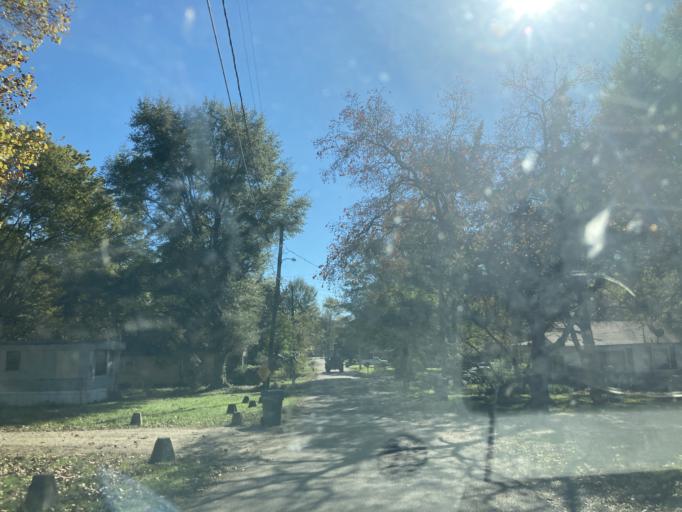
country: US
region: Mississippi
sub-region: Yazoo County
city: Yazoo City
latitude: 32.8444
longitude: -90.4305
